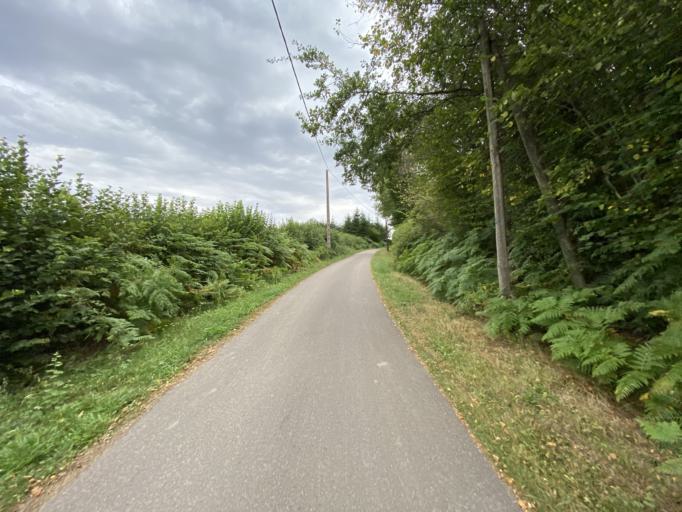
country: FR
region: Bourgogne
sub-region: Departement de la Cote-d'Or
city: Saulieu
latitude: 47.2699
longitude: 4.1462
